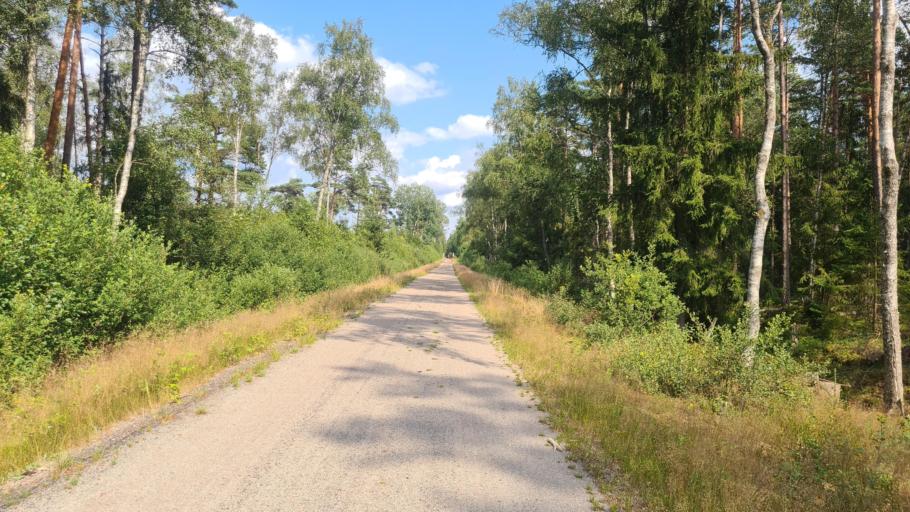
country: SE
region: Kronoberg
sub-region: Ljungby Kommun
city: Ljungby
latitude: 56.8511
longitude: 14.0013
